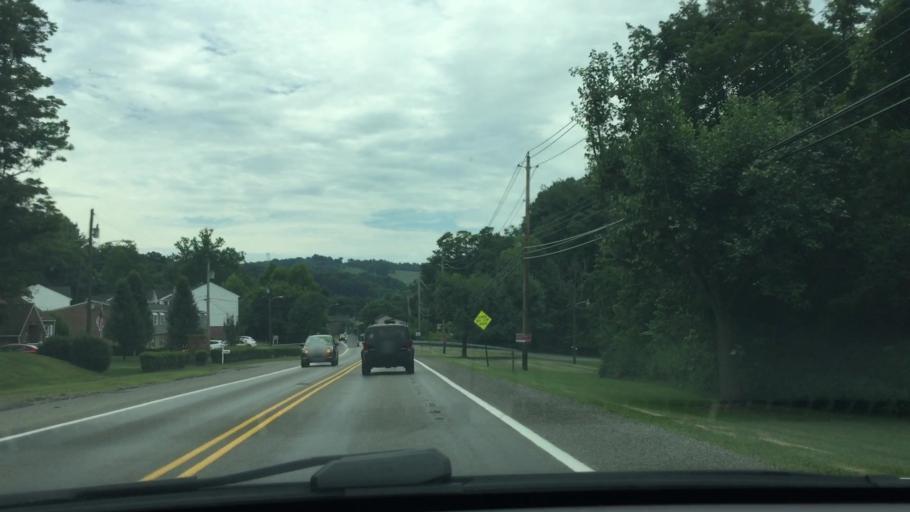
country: US
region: Pennsylvania
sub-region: Allegheny County
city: Oakdale
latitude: 40.4032
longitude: -80.1896
